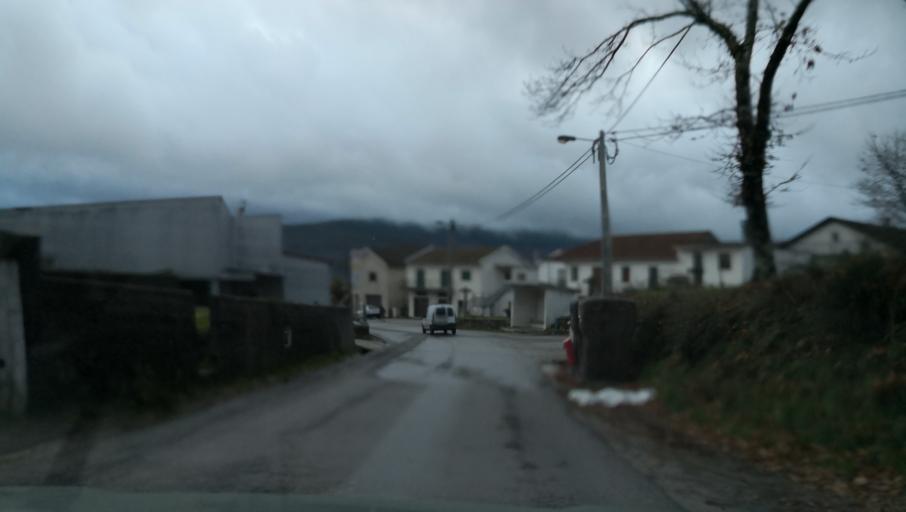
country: PT
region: Vila Real
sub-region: Santa Marta de Penaguiao
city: Santa Marta de Penaguiao
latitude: 41.3019
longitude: -7.8705
